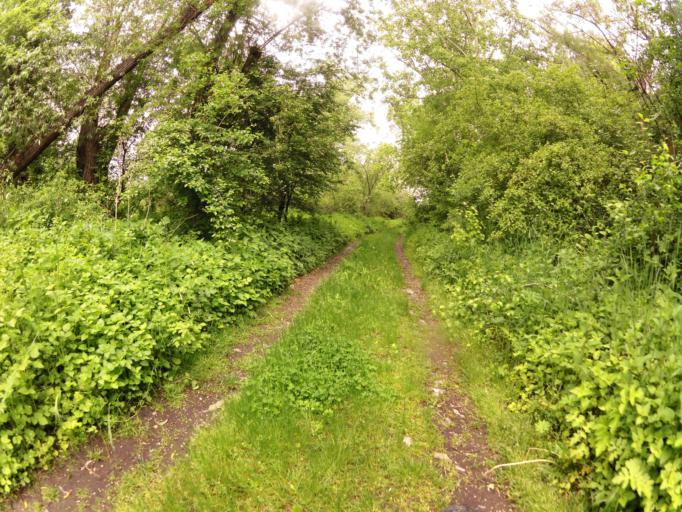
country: DE
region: Bavaria
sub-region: Regierungsbezirk Unterfranken
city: Sommerach
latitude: 49.8144
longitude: 10.2186
